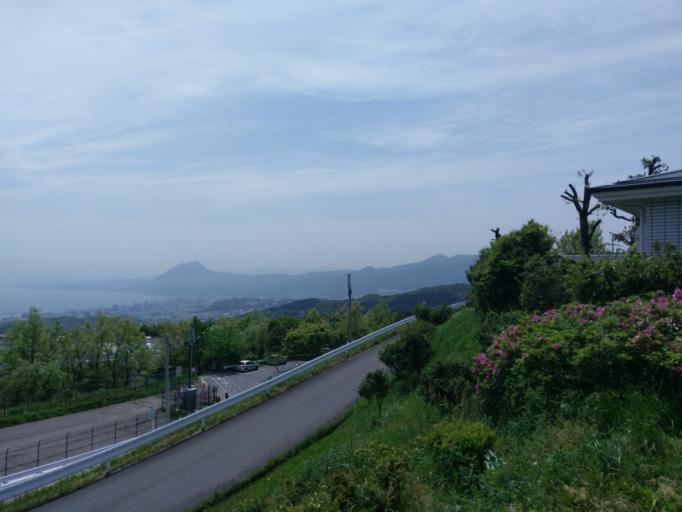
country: JP
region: Oita
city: Beppu
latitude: 33.3365
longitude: 131.4652
